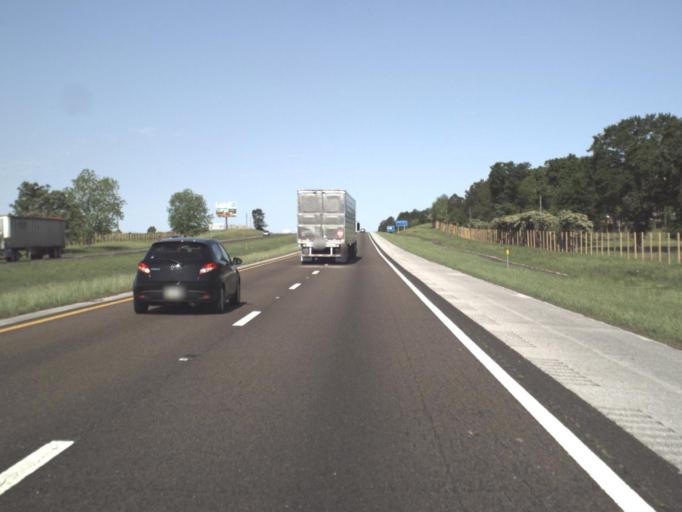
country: US
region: Florida
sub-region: Holmes County
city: Bonifay
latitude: 30.7622
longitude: -85.6630
